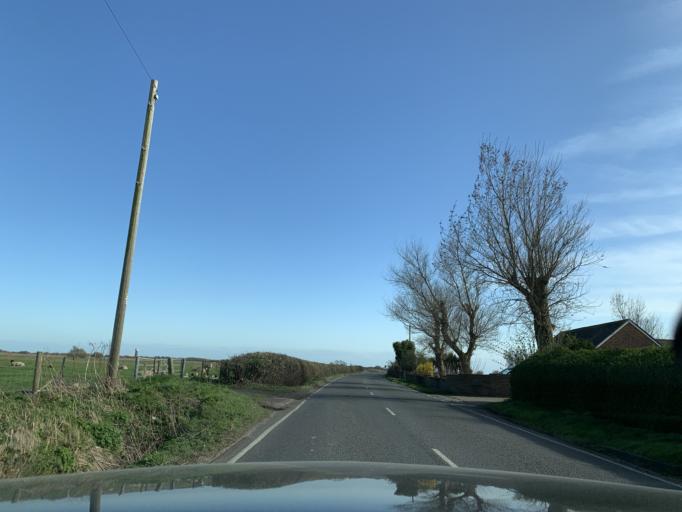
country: GB
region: England
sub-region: Kent
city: Lydd
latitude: 50.9499
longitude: 0.9158
